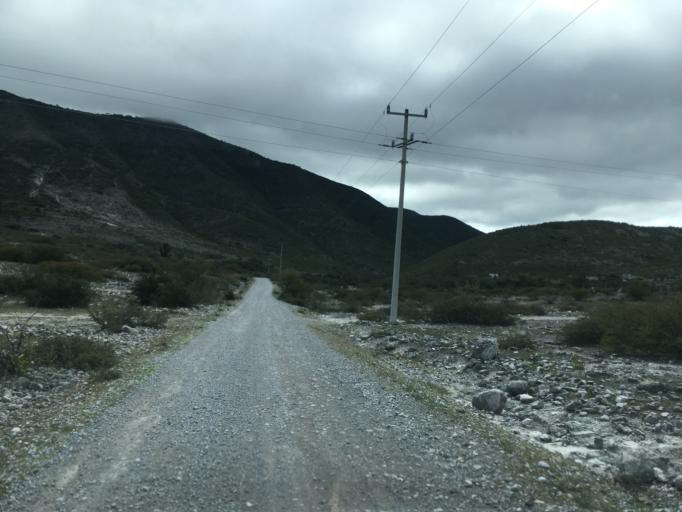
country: MX
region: Hidalgo
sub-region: Metztitlan
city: Fontezuelas
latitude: 20.6295
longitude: -98.8587
